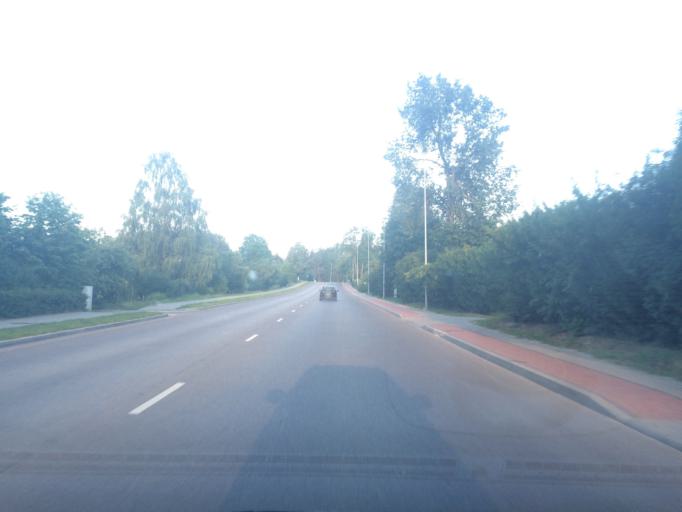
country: LT
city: Zarasai
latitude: 55.7199
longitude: 26.2356
